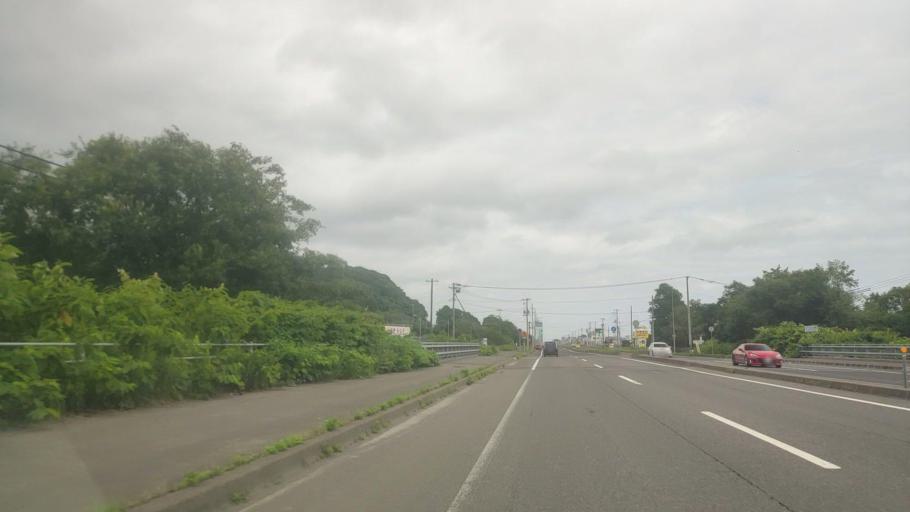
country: JP
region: Hokkaido
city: Shiraoi
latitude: 42.4601
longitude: 141.2047
